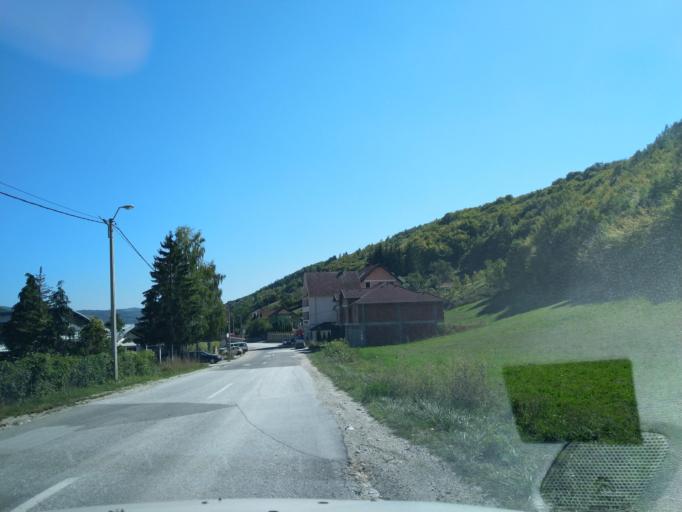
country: RS
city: Sokolovica
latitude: 43.2502
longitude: 20.2589
